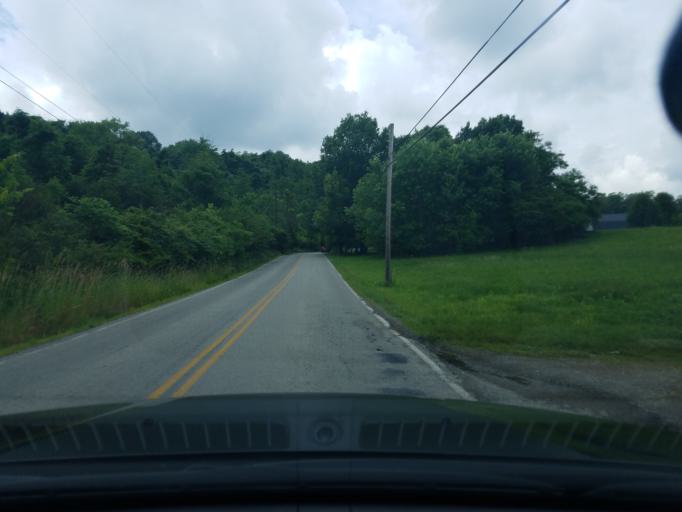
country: US
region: Pennsylvania
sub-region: Westmoreland County
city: Youngwood
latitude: 40.2190
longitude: -79.5553
